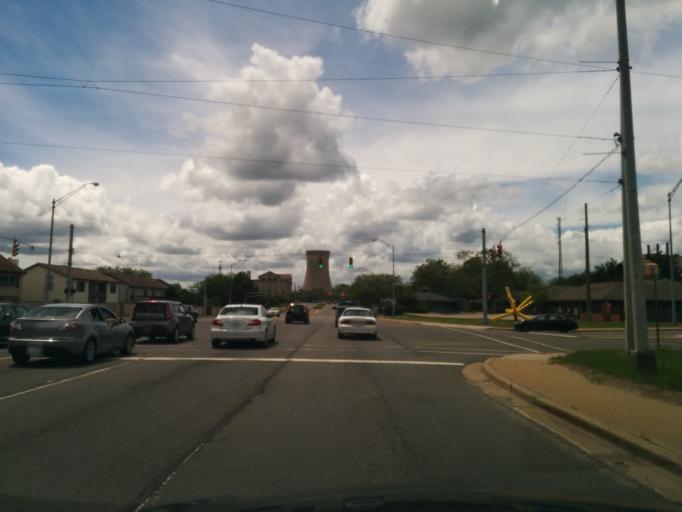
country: US
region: Indiana
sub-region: LaPorte County
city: Michigan City
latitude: 41.7205
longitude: -86.8996
